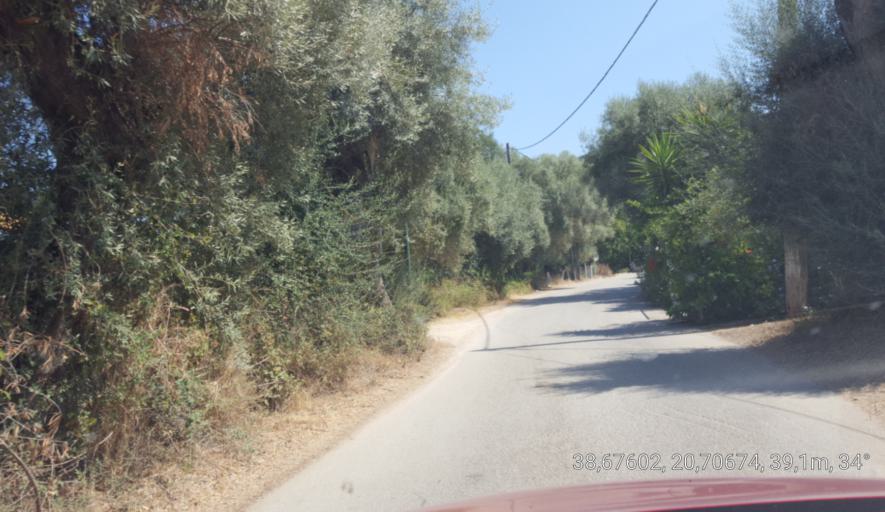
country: GR
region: Ionian Islands
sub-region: Lefkada
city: Nidri
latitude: 38.6761
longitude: 20.7067
